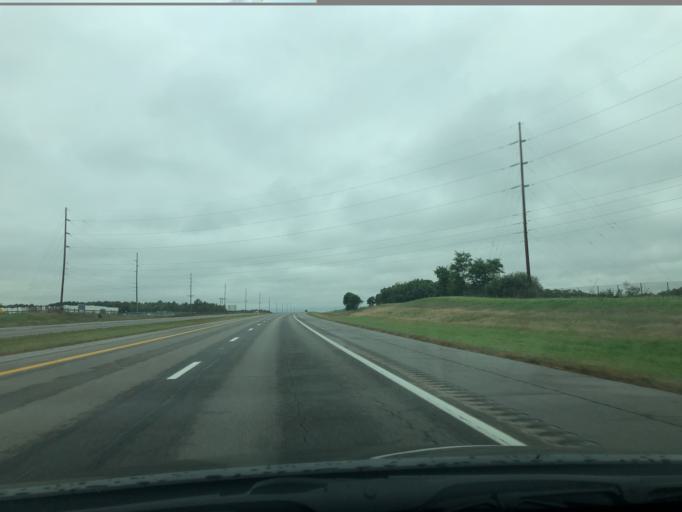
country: US
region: Ohio
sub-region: Champaign County
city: North Lewisburg
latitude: 40.2827
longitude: -83.5460
